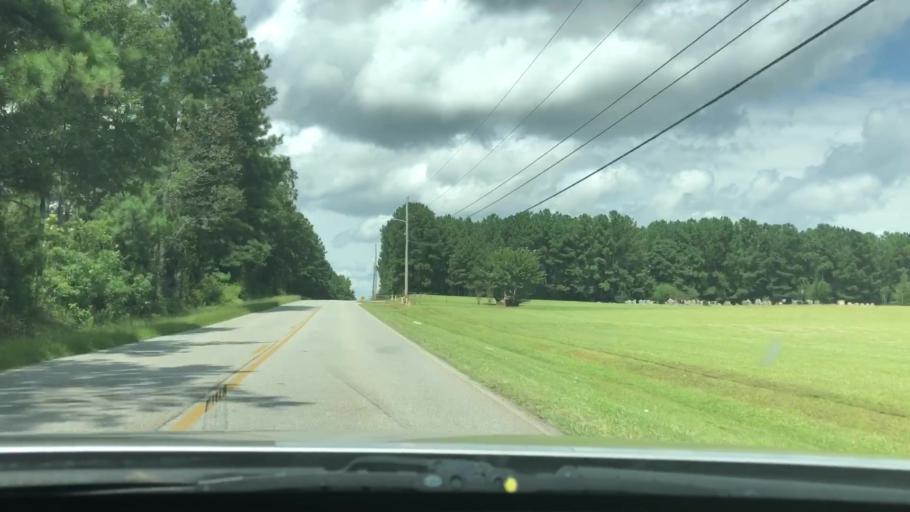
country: US
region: Georgia
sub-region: Henry County
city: McDonough
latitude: 33.4064
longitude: -84.1195
